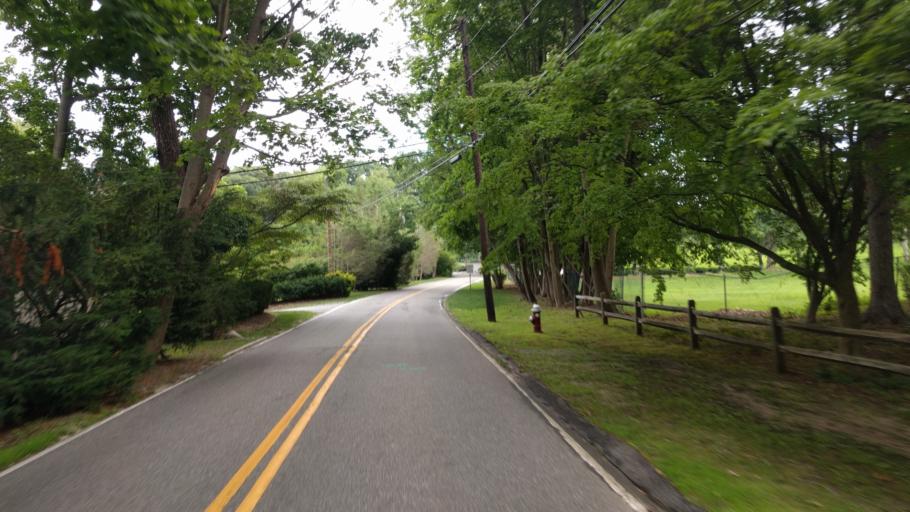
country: US
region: New York
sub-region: Nassau County
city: Oyster Bay Cove
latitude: 40.8682
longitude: -73.5213
